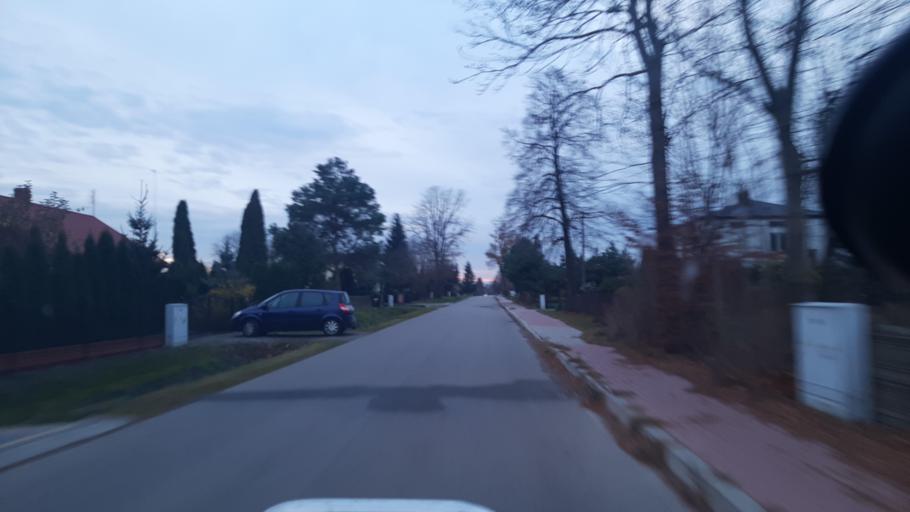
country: PL
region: Lublin Voivodeship
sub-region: Powiat lubelski
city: Garbow
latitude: 51.3629
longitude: 22.3800
